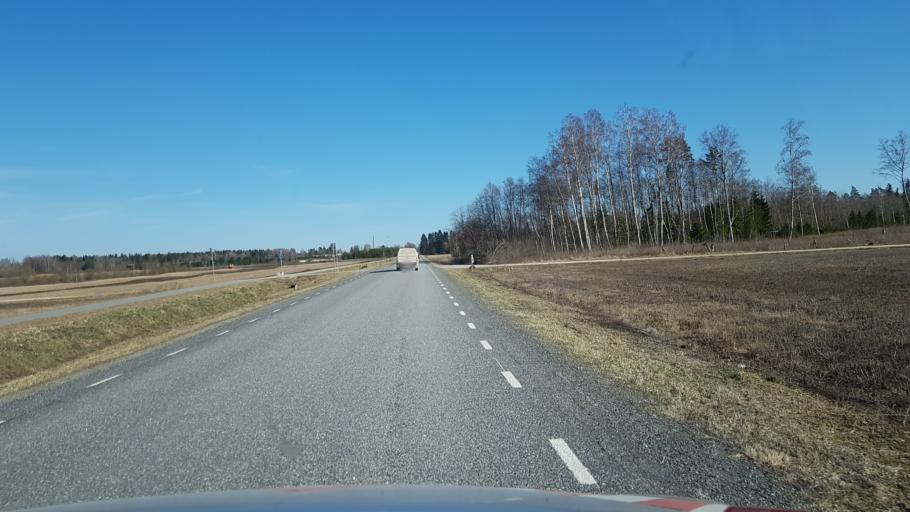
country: EE
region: Laeaene-Virumaa
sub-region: Rakke vald
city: Rakke
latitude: 58.9973
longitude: 26.2099
